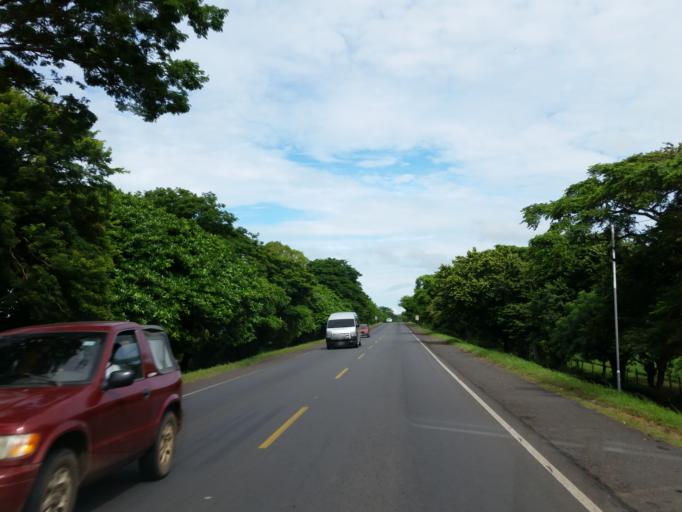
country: NI
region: Leon
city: Nagarote
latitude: 12.3076
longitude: -86.6019
